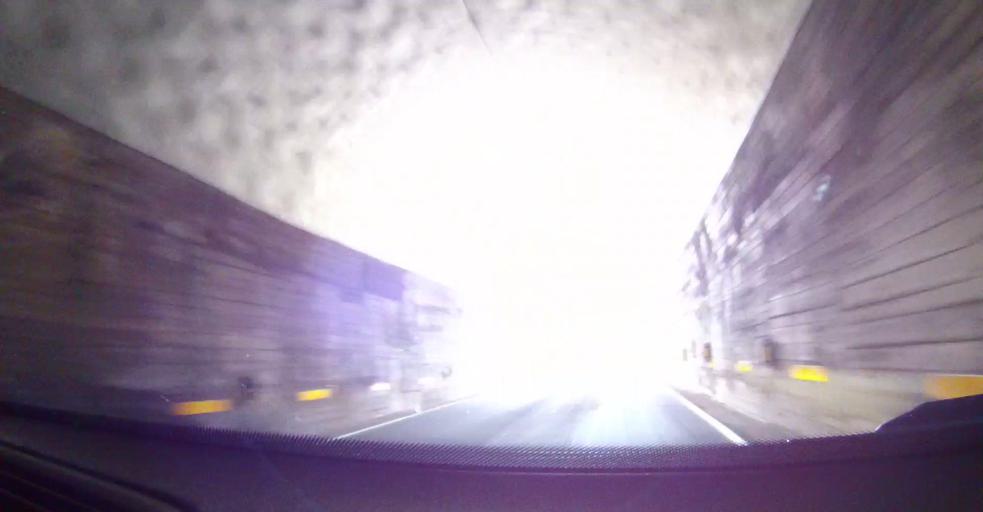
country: ES
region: Castille and Leon
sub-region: Provincia de Leon
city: Puebla de Lillo
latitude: 42.9711
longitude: -5.2575
